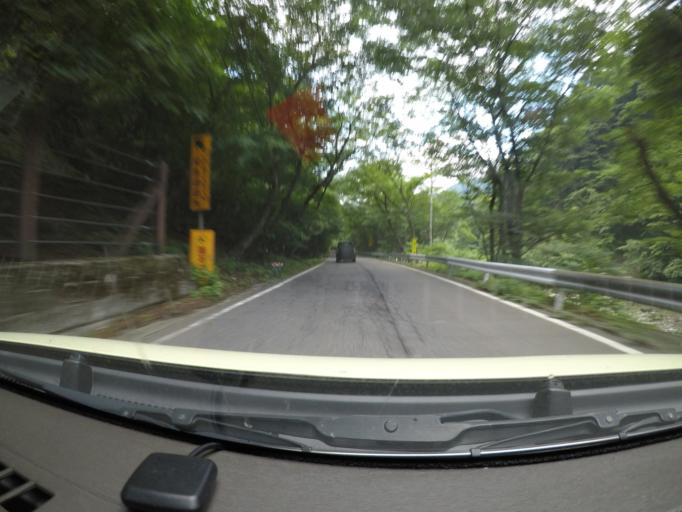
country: JP
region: Tochigi
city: Nikko
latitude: 36.7412
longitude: 139.5236
